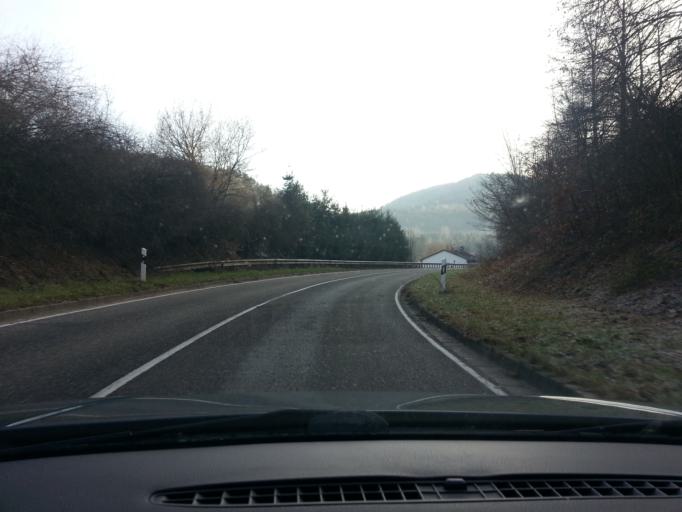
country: DE
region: Rheinland-Pfalz
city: Lug
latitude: 49.1813
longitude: 7.8953
